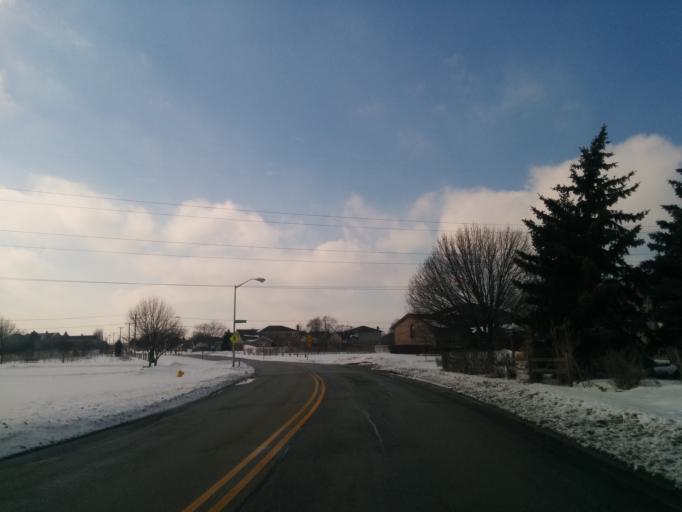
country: US
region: Illinois
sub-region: Cook County
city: Orland Hills
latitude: 41.5726
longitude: -87.8163
